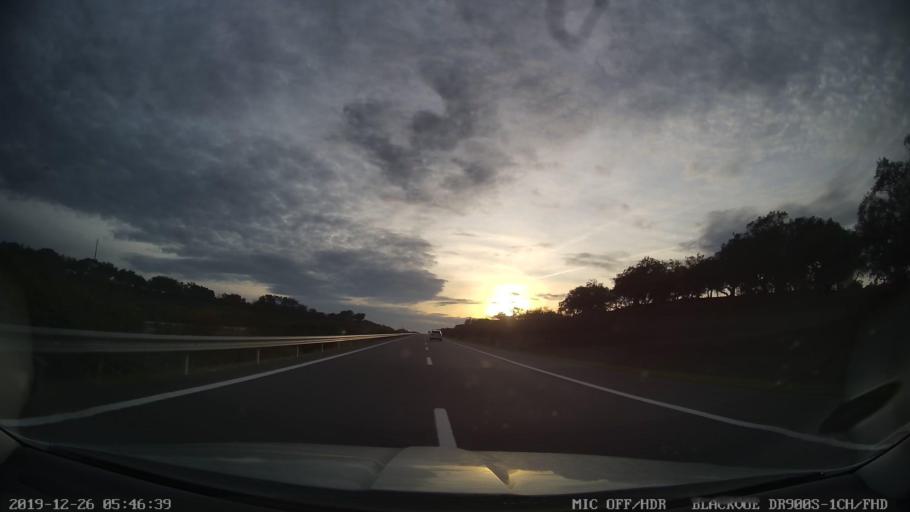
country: PT
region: Evora
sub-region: Estremoz
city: Estremoz
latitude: 38.7378
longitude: -7.7614
